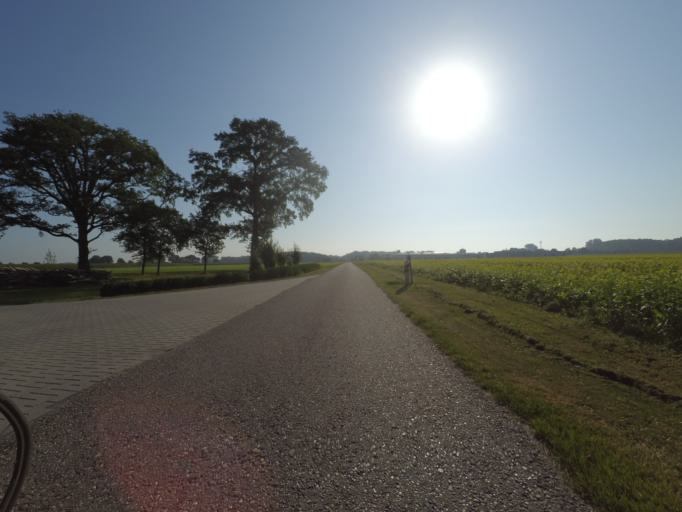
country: DE
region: Lower Saxony
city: Ohne
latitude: 52.2460
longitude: 7.2868
